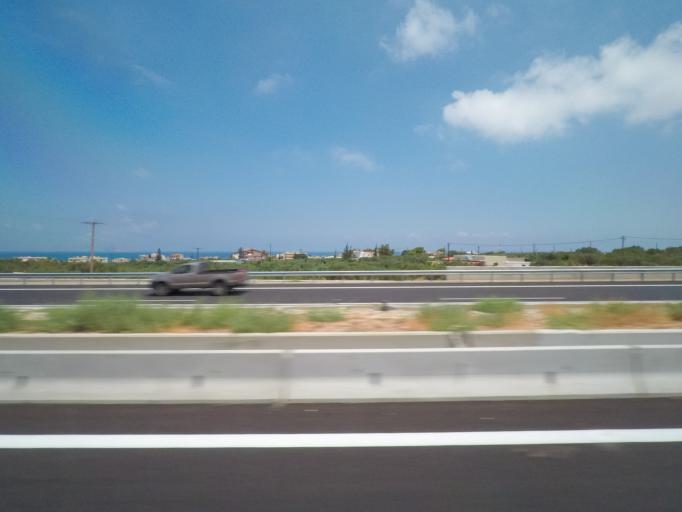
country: GR
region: Crete
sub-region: Nomos Irakleiou
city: Gouvai
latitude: 35.3238
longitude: 25.2998
